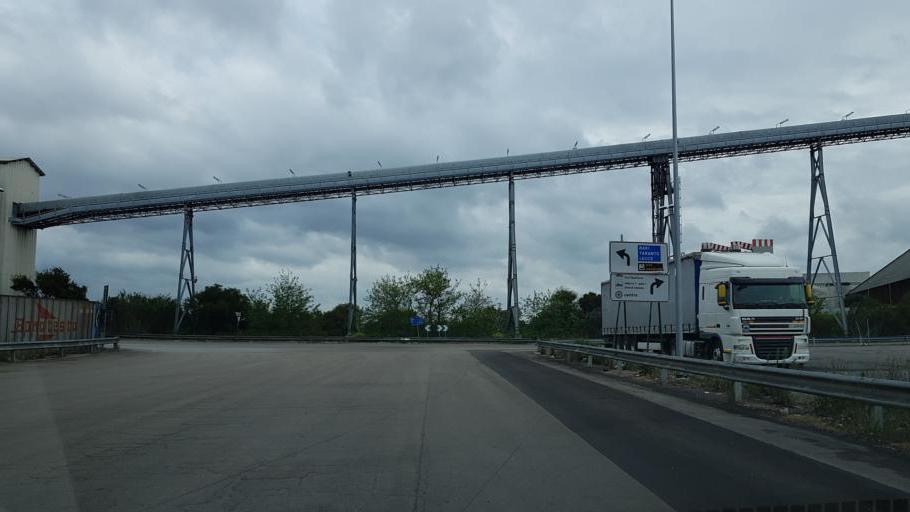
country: IT
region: Apulia
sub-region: Provincia di Brindisi
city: Materdomini
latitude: 40.6413
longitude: 17.9628
